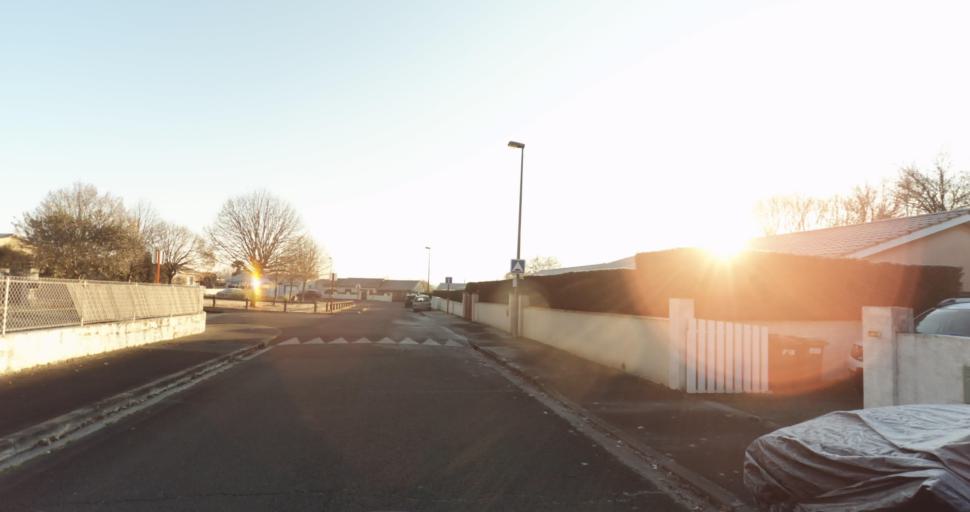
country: FR
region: Aquitaine
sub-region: Departement de la Gironde
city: Ambares-et-Lagrave
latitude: 44.9139
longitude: -0.4965
